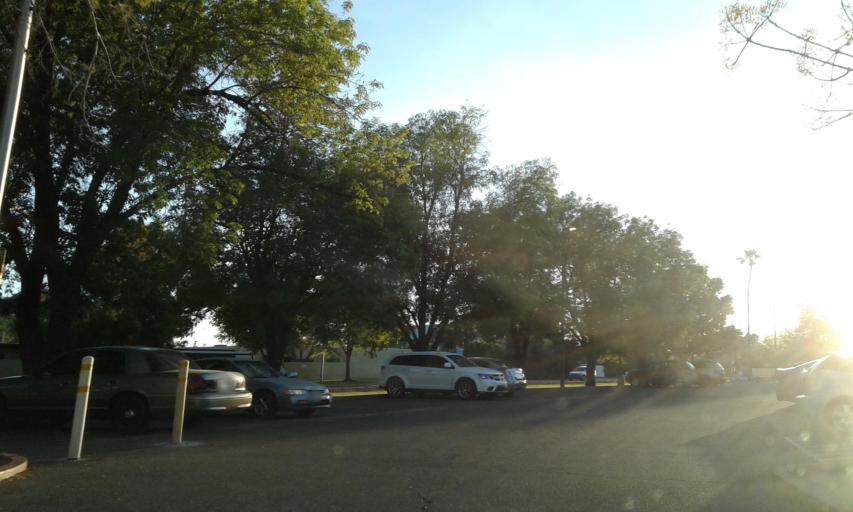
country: US
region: Arizona
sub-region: Maricopa County
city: Glendale
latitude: 33.5300
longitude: -112.1065
